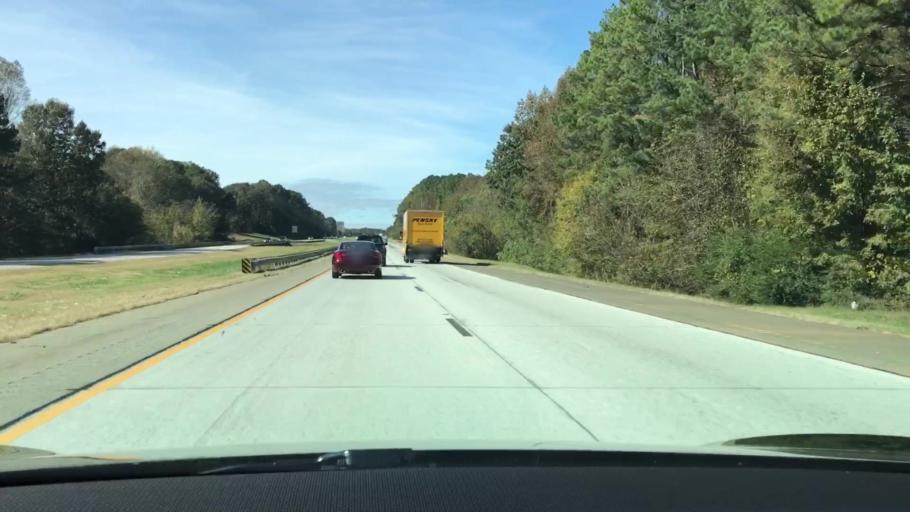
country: US
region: Georgia
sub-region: Morgan County
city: Madison
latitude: 33.5546
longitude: -83.3899
